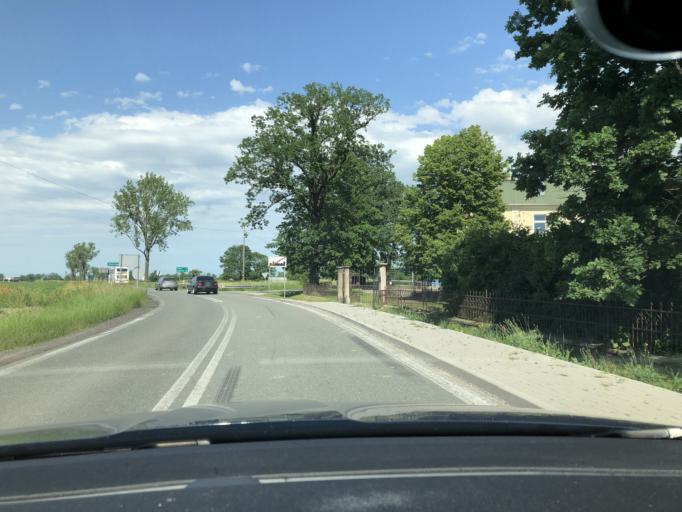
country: PL
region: Lower Silesian Voivodeship
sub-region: Powiat jaworski
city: Paszowice
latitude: 50.9780
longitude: 16.1609
